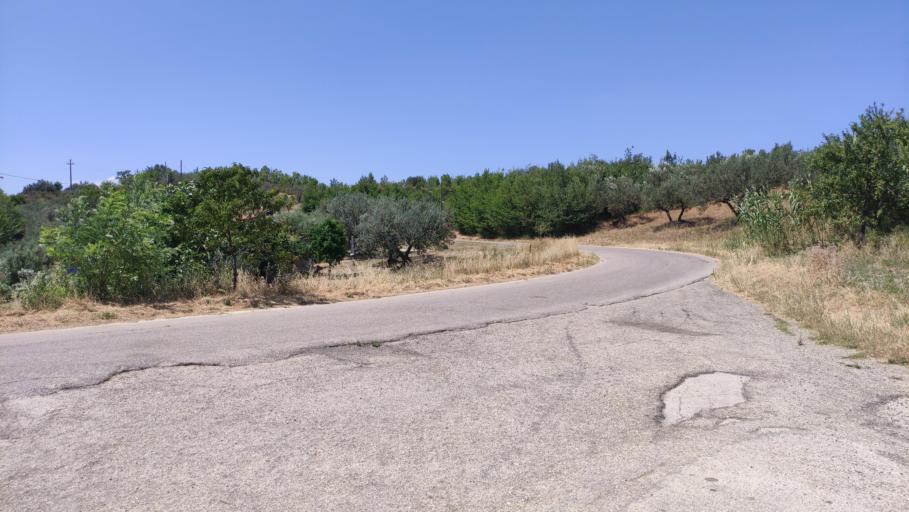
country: IT
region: Abruzzo
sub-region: Provincia di Pescara
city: Serramonacesca
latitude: 42.2567
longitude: 14.0906
